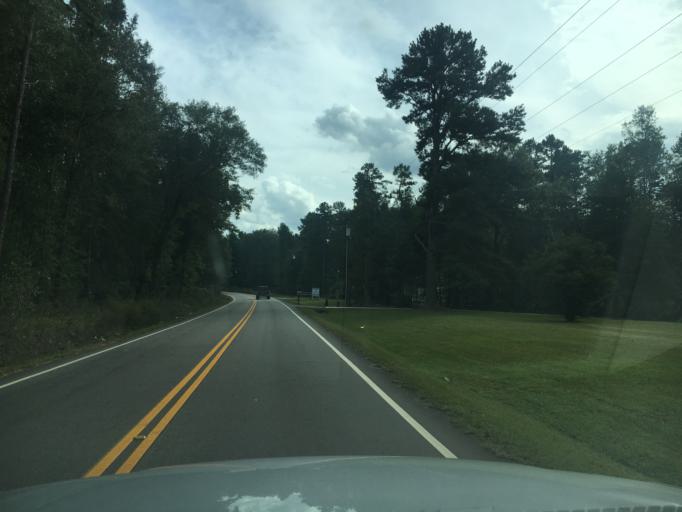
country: US
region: South Carolina
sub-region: Spartanburg County
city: Wellford
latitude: 34.9242
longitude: -82.0627
